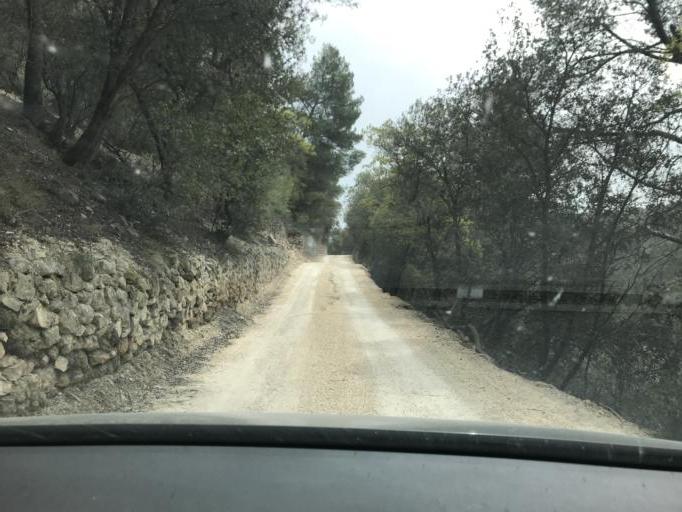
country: ES
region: Andalusia
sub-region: Provincia de Granada
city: Castril
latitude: 37.8376
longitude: -2.7731
